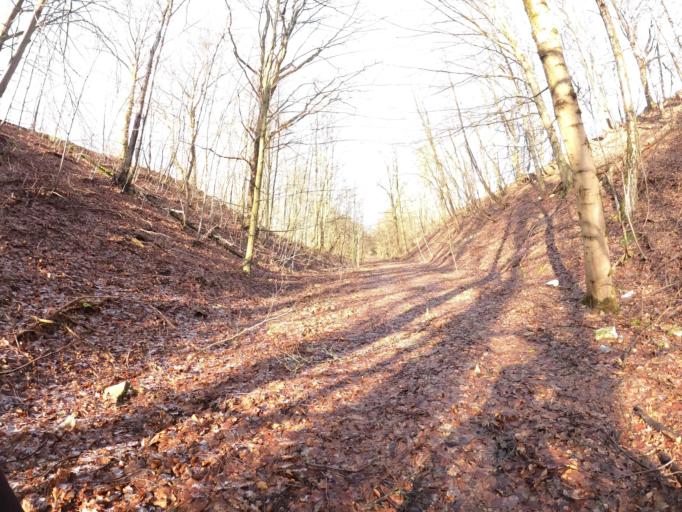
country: PL
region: West Pomeranian Voivodeship
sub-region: Powiat koszalinski
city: Polanow
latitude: 54.1392
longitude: 16.7714
